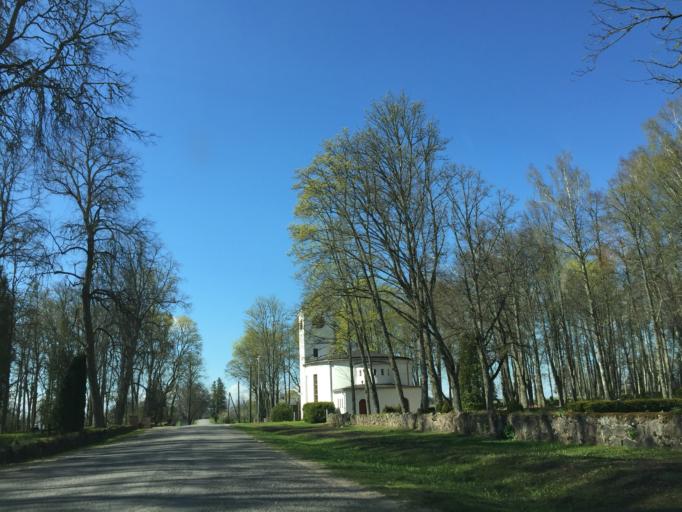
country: LV
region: Strenci
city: Strenci
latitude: 57.5433
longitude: 25.7044
